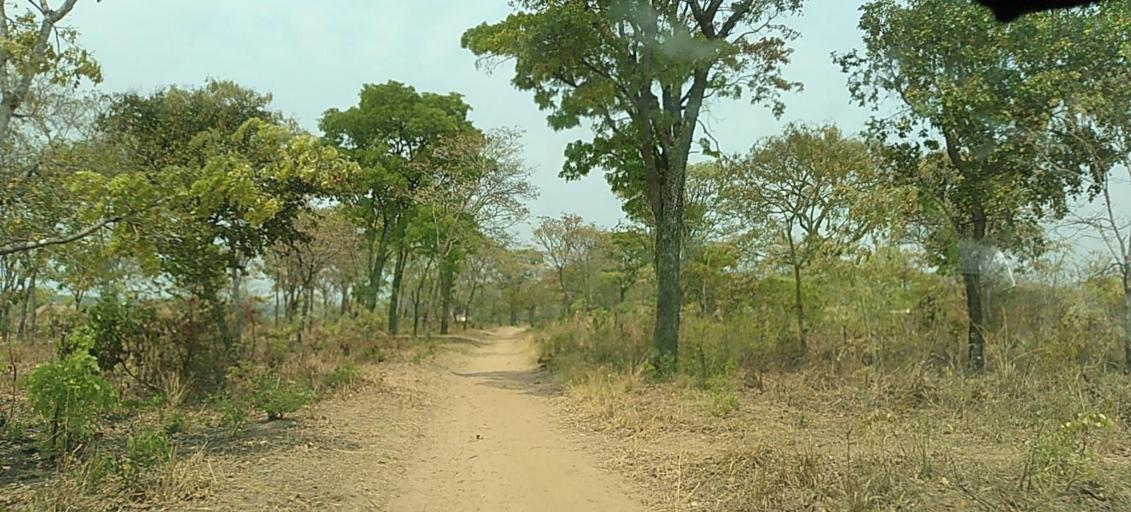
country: ZM
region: North-Western
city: Kabompo
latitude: -13.5318
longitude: 24.4614
